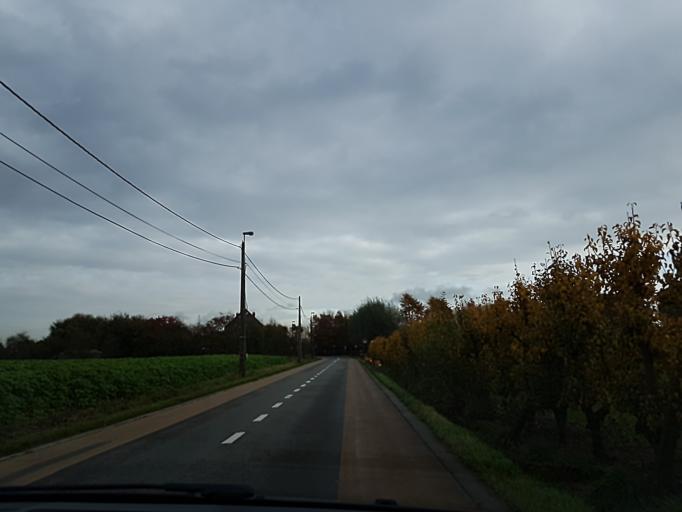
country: BE
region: Flanders
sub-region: Provincie Antwerpen
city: Ranst
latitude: 51.1723
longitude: 4.5516
